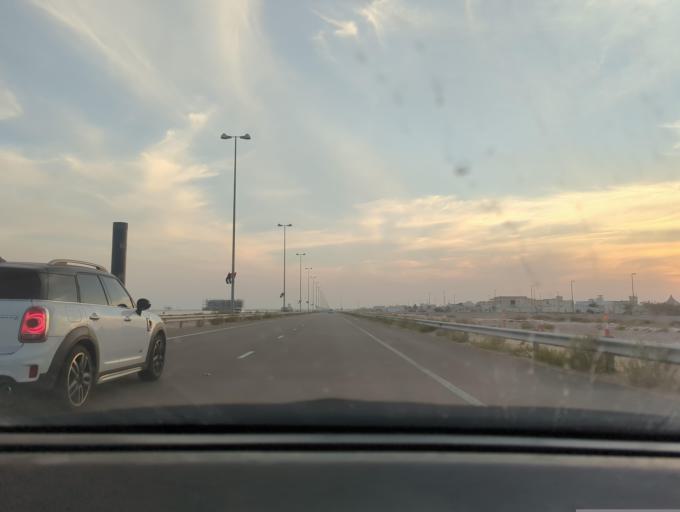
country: AE
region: Abu Dhabi
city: Abu Dhabi
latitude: 24.3538
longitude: 54.6629
